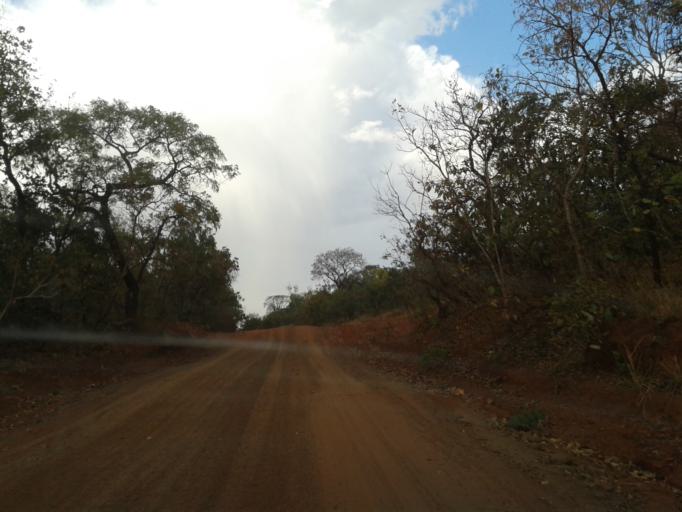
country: BR
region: Minas Gerais
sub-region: Santa Vitoria
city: Santa Vitoria
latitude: -19.1947
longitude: -49.8814
